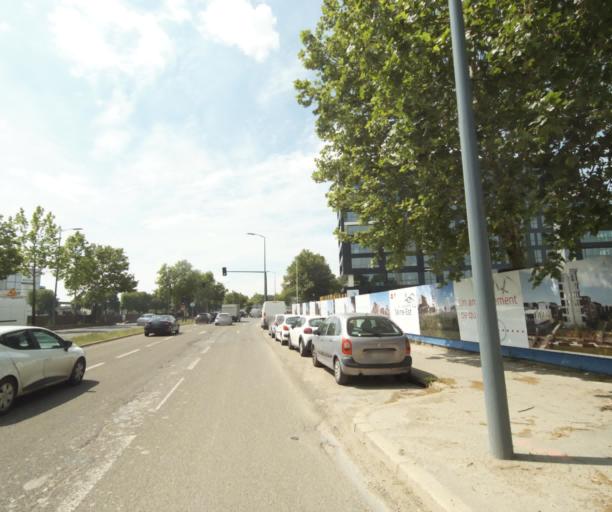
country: FR
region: Ile-de-France
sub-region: Departement des Hauts-de-Seine
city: Clichy
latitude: 48.9180
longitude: 2.3203
